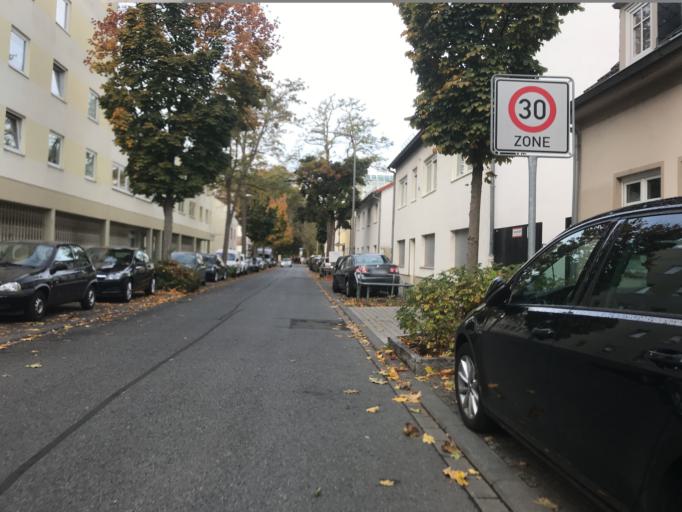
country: DE
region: Hesse
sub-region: Regierungsbezirk Darmstadt
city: Wiesbaden
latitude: 50.0401
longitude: 8.2387
